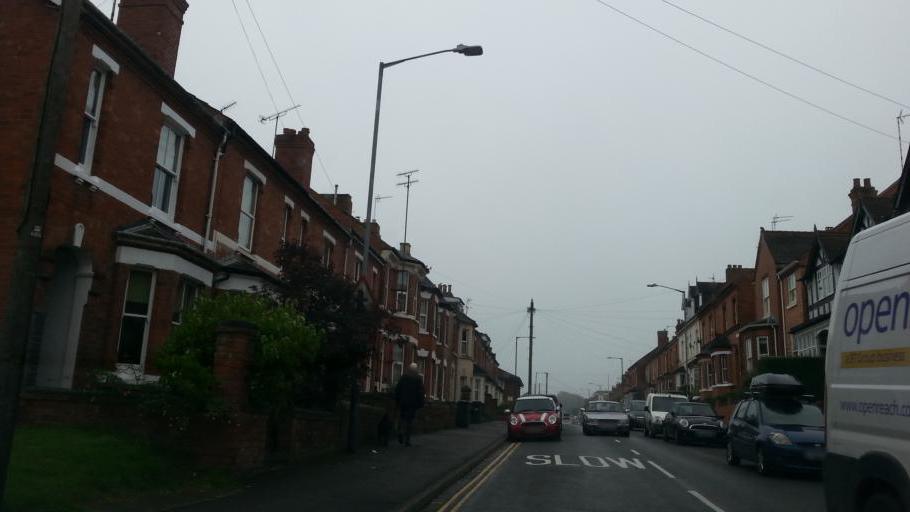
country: GB
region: England
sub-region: Warwickshire
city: Kenilworth
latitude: 52.3511
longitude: -1.5706
